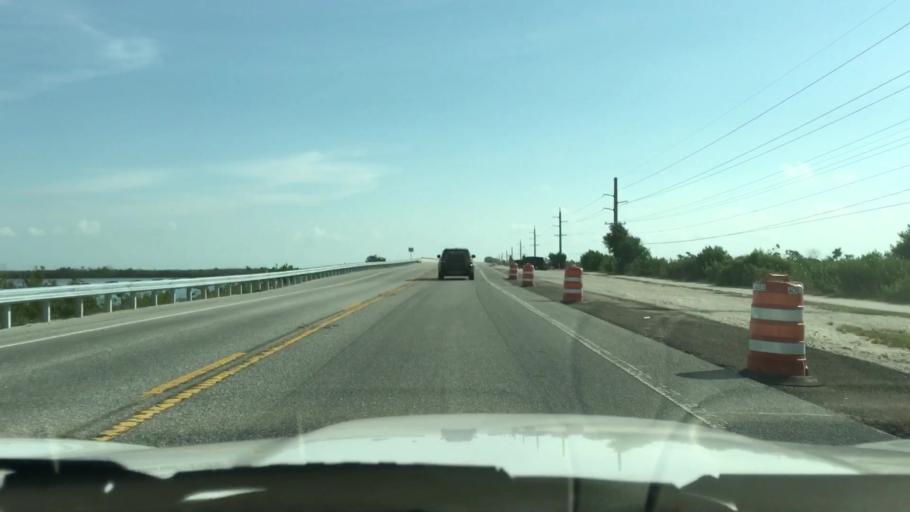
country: US
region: Florida
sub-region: Monroe County
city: Cudjoe Key
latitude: 24.6629
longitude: -81.4690
